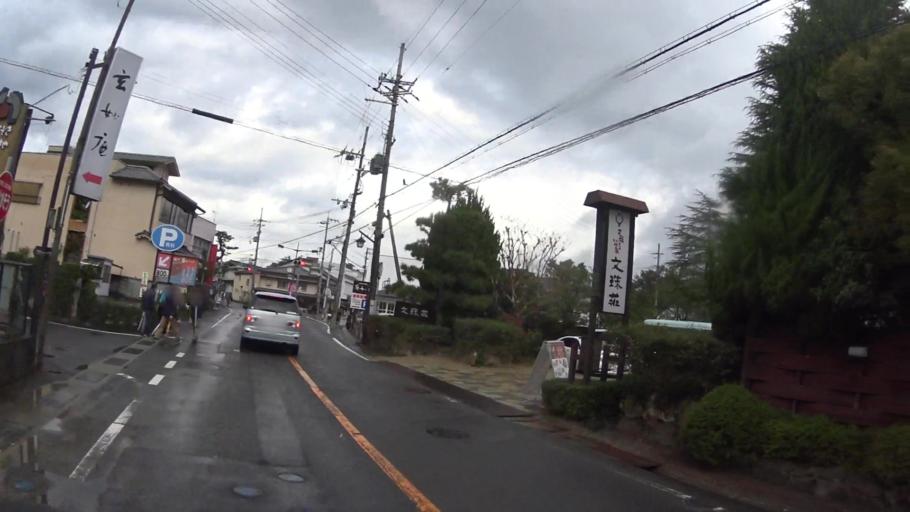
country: JP
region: Kyoto
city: Miyazu
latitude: 35.5560
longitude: 135.1842
